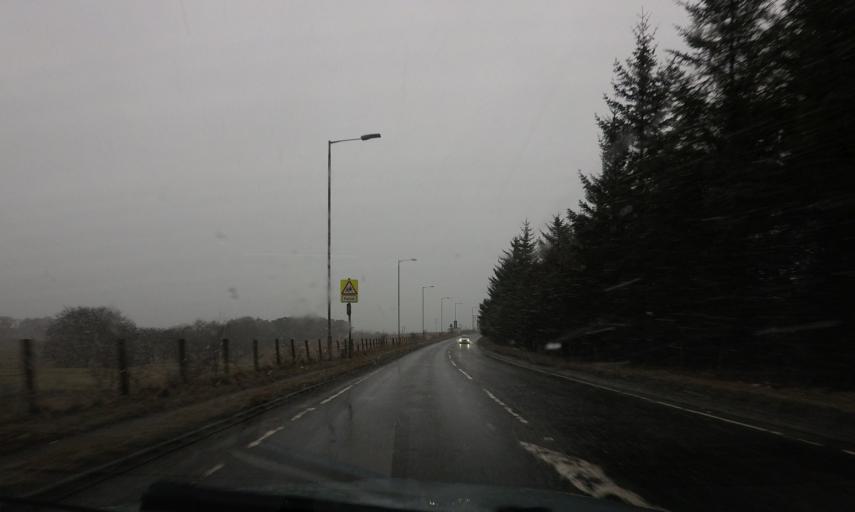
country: GB
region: Scotland
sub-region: North Lanarkshire
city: Caldercruix
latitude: 55.8461
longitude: -3.8541
